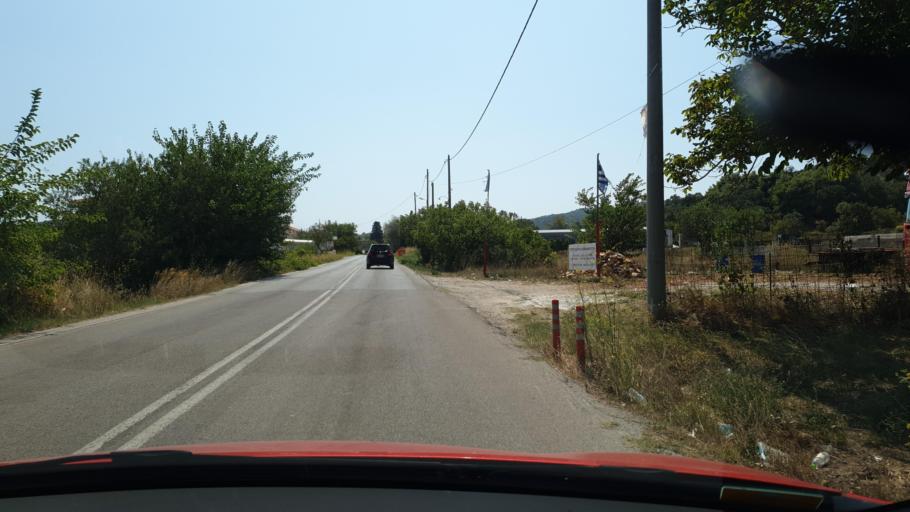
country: GR
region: Central Greece
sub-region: Nomos Evvoias
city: Oxilithos
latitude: 38.5054
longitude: 24.1096
